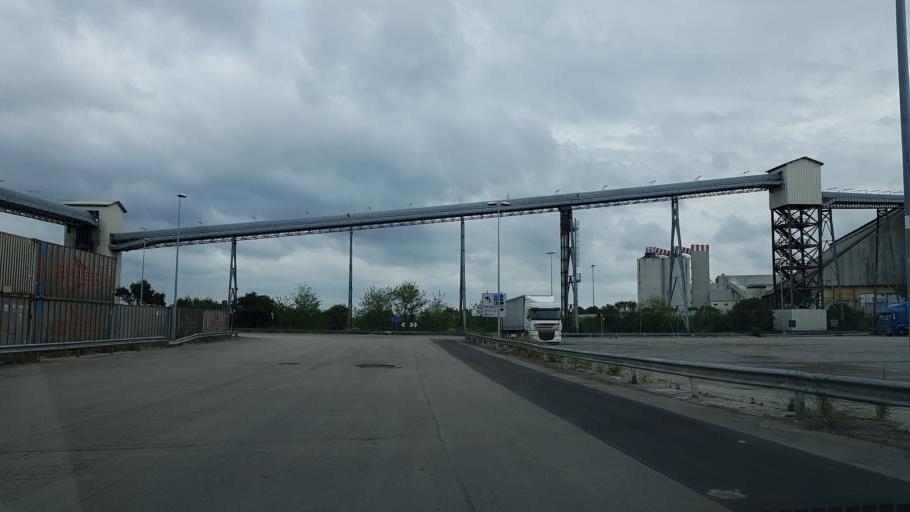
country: IT
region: Apulia
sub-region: Provincia di Brindisi
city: Materdomini
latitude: 40.6416
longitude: 17.9627
